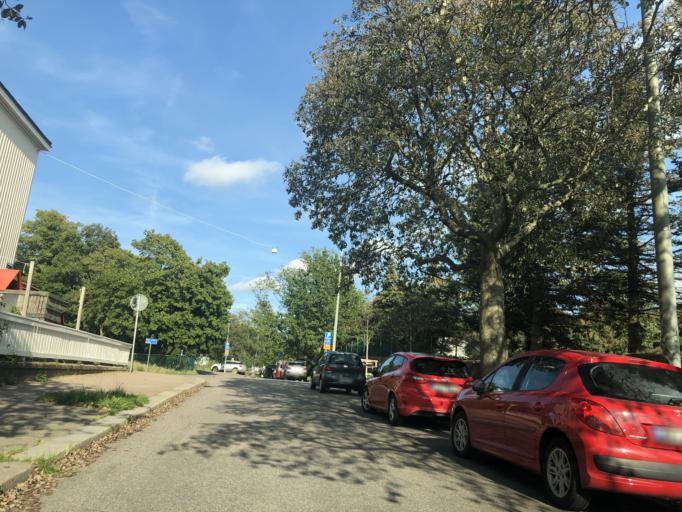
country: SE
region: Vaestra Goetaland
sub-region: Goteborg
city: Majorna
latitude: 57.6841
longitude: 11.9202
